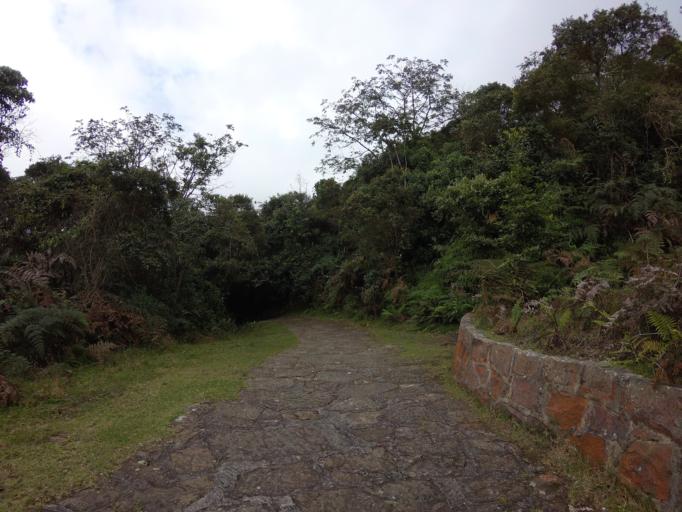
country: CO
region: Cundinamarca
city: San Antonio del Tequendama
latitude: 4.6075
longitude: -74.3068
